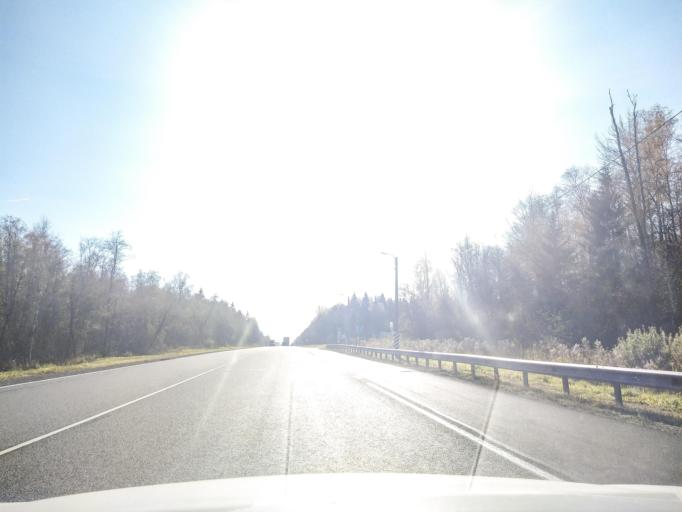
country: RU
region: Leningrad
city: Rozhdestveno
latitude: 59.3891
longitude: 29.9705
